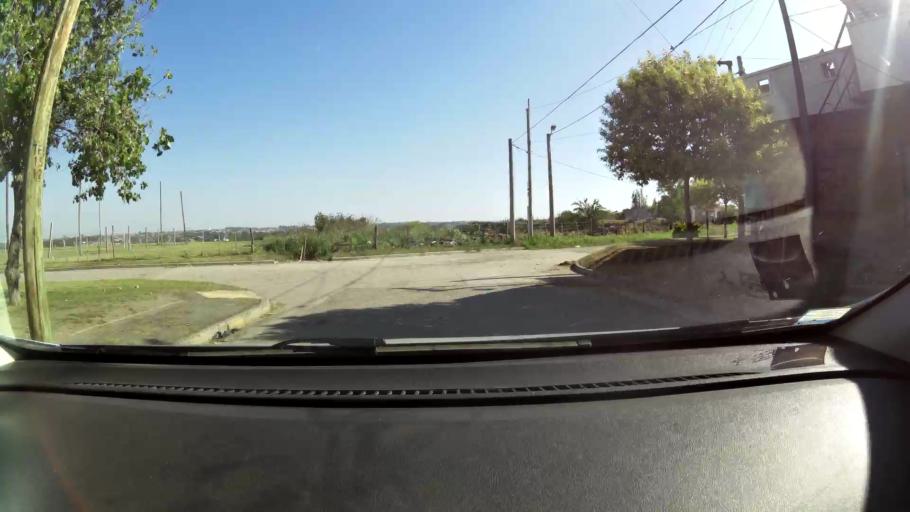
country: AR
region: Cordoba
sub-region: Departamento de Capital
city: Cordoba
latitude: -31.3954
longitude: -64.1447
